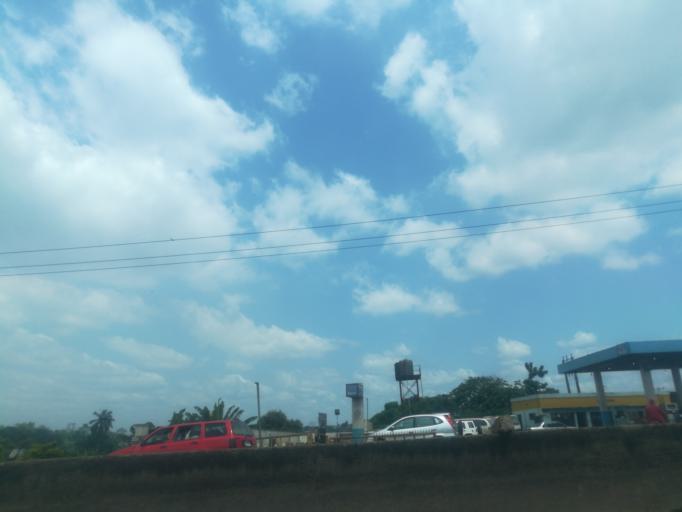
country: NG
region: Oyo
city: Ibadan
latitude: 7.3916
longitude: 3.9737
